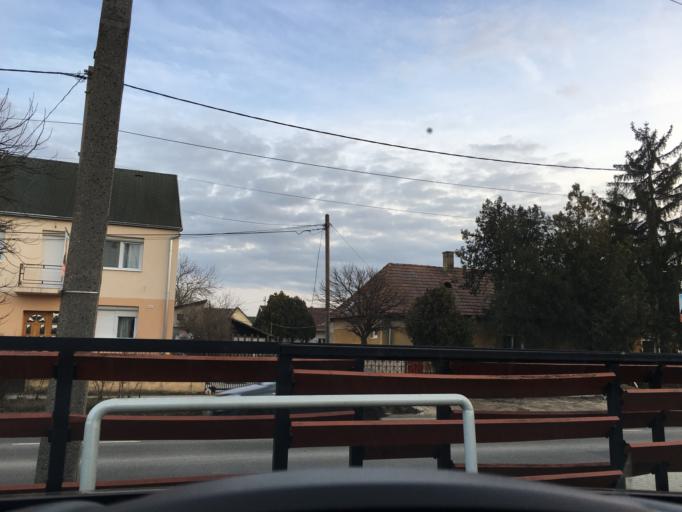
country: HU
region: Budapest
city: Budapest XVII. keruelet
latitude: 47.4865
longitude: 19.2850
